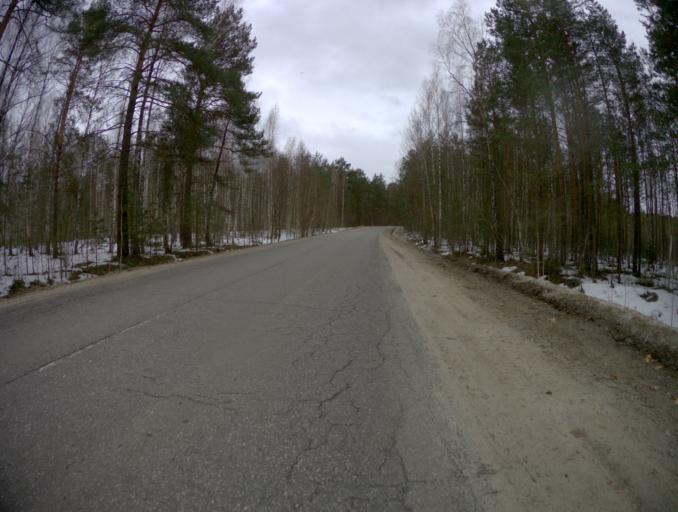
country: RU
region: Vladimir
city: Bogolyubovo
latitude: 56.1488
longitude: 40.5277
